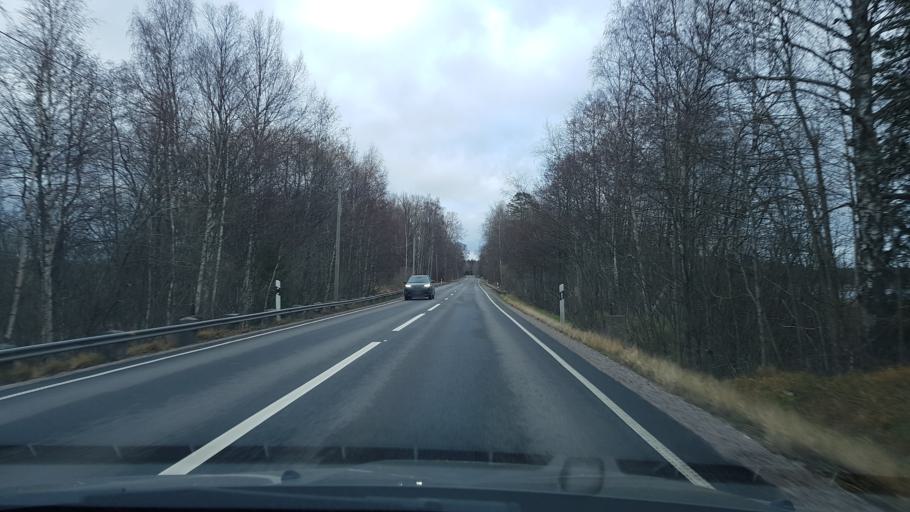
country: SE
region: Stockholm
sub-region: Norrtalje Kommun
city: Skanninge
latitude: 60.0119
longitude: 18.3374
